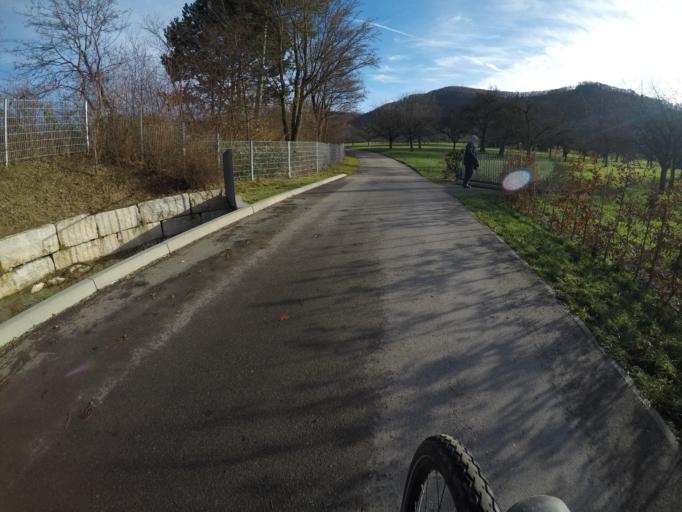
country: DE
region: Baden-Wuerttemberg
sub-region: Regierungsbezirk Stuttgart
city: Beuren
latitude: 48.5650
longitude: 9.3982
